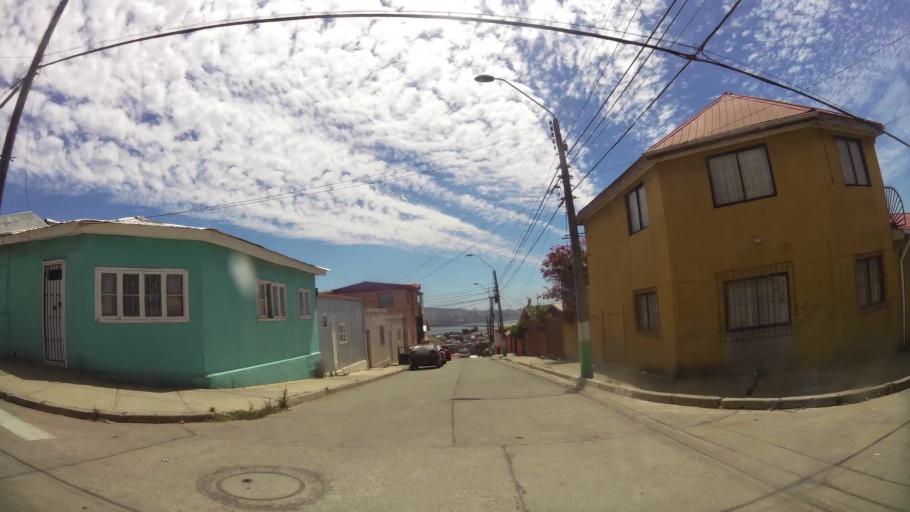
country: CL
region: Valparaiso
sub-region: Provincia de Valparaiso
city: Vina del Mar
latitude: -33.0361
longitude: -71.5836
